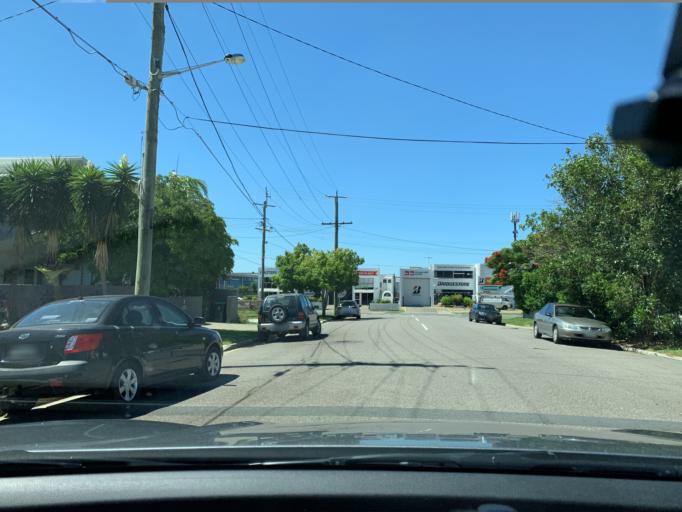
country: AU
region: Queensland
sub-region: Brisbane
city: Ascot
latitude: -27.4197
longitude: 153.0727
